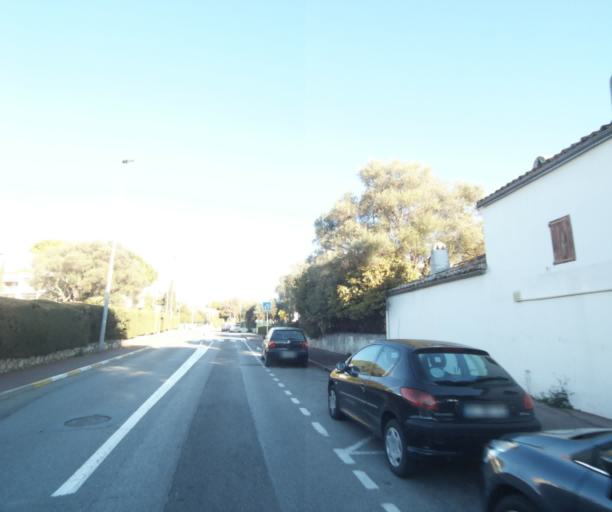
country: FR
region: Provence-Alpes-Cote d'Azur
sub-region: Departement des Alpes-Maritimes
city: Antibes
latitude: 43.5799
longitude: 7.0984
